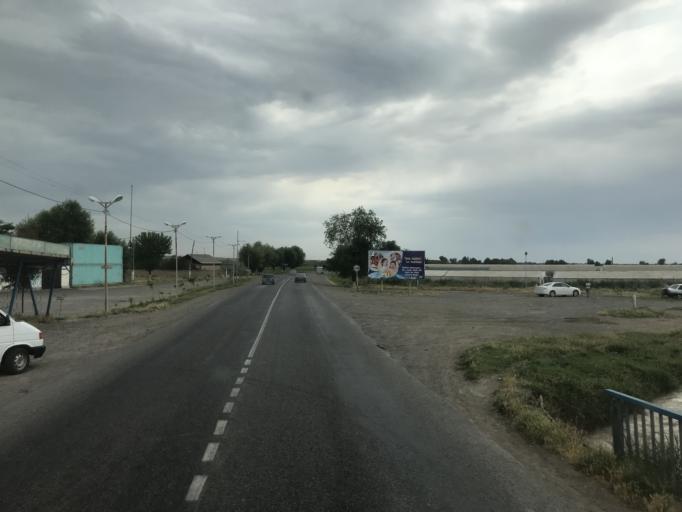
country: KZ
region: Ongtustik Qazaqstan
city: Saryaghash
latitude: 41.3703
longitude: 68.9959
